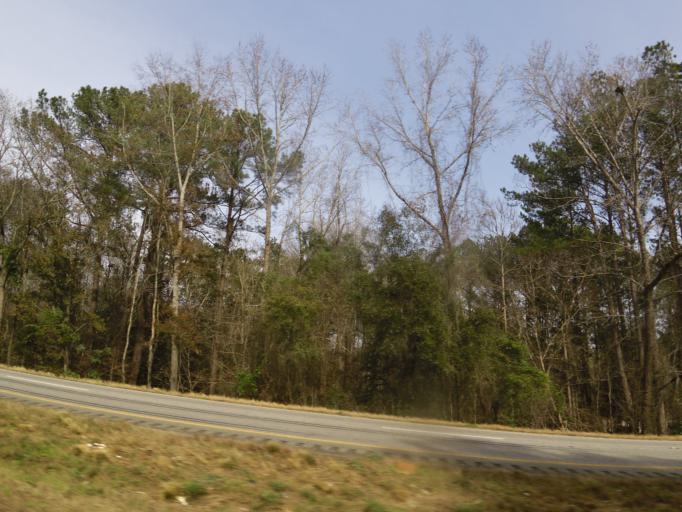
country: US
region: Alabama
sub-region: Dale County
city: Midland City
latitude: 31.3346
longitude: -85.5403
